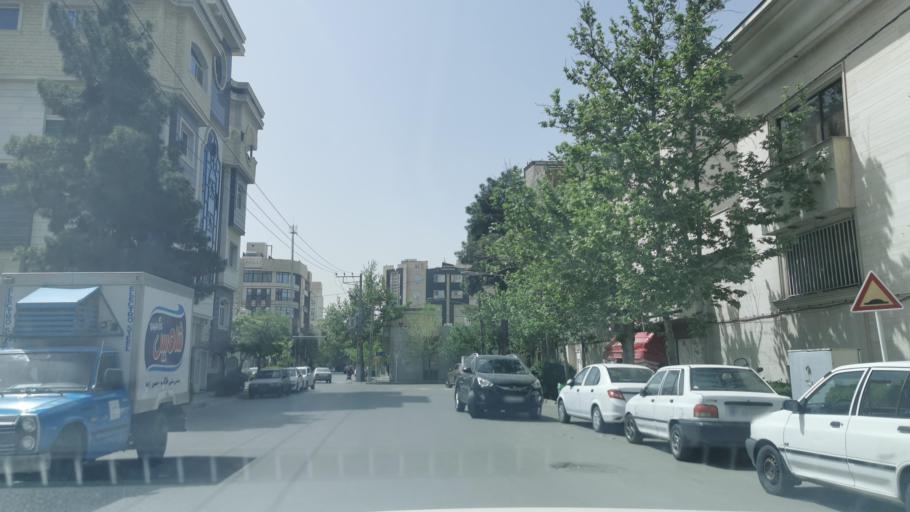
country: IR
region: Razavi Khorasan
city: Mashhad
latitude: 36.3090
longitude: 59.5604
